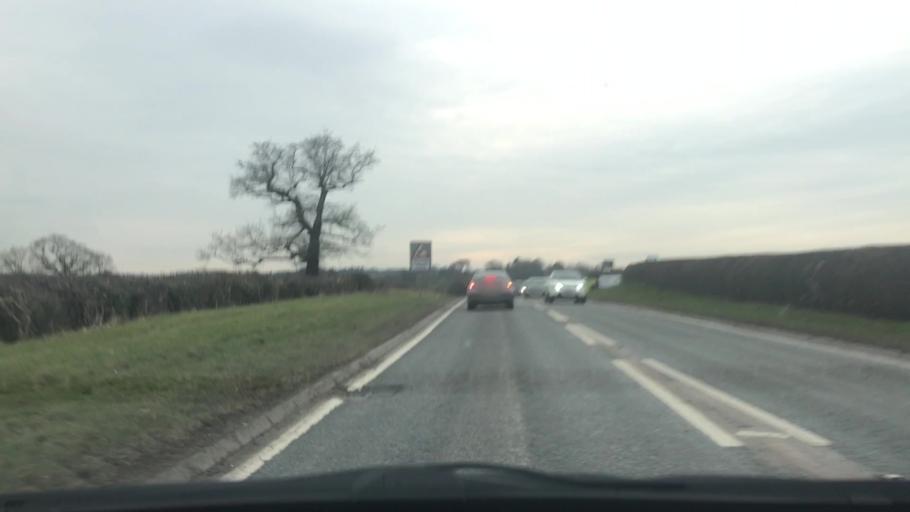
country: GB
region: England
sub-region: North Yorkshire
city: Knaresborough
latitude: 53.9813
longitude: -1.4786
